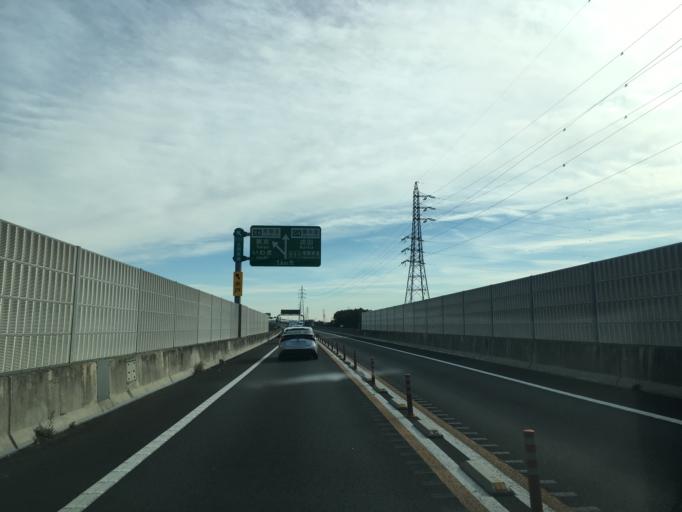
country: JP
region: Ibaraki
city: Naka
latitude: 36.0388
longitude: 140.1147
